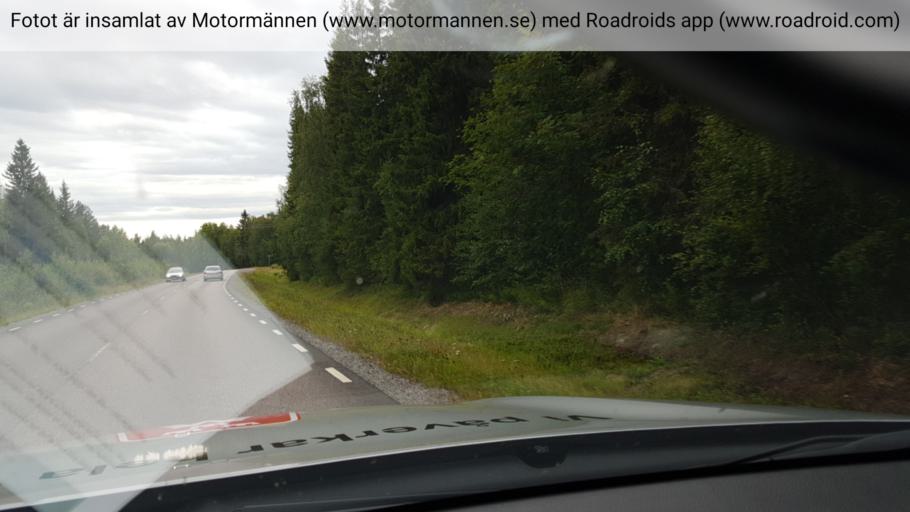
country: SE
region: Norrbotten
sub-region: Lulea Kommun
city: Gammelstad
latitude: 65.6547
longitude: 22.0363
